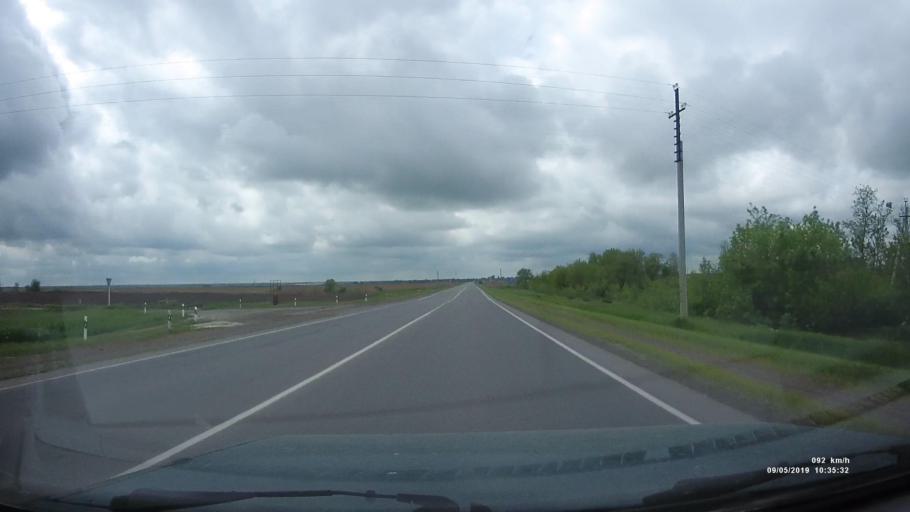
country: RU
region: Rostov
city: Peshkovo
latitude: 47.0414
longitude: 39.4132
